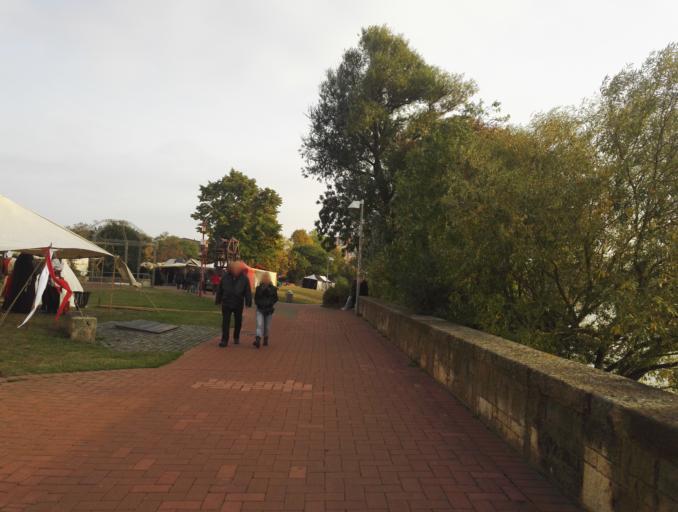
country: DE
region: Lower Saxony
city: Hameln
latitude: 52.1005
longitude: 9.3537
